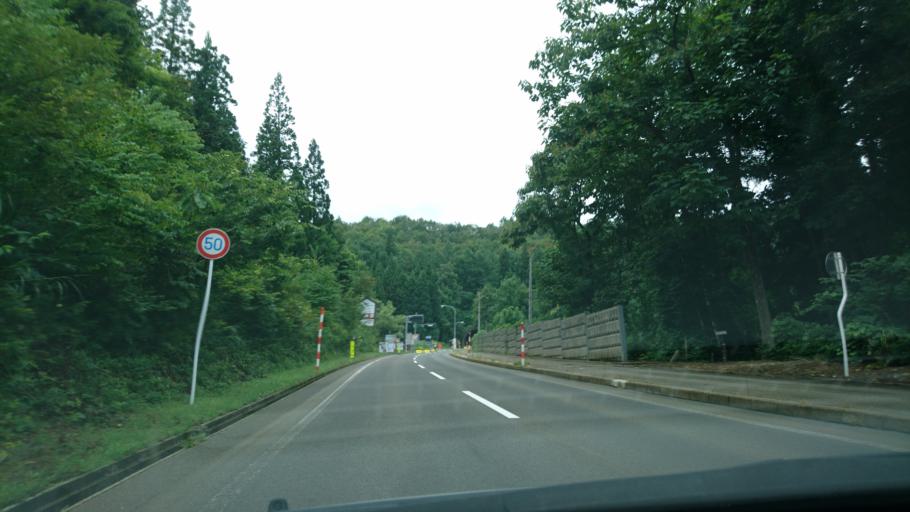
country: JP
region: Akita
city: Yuzawa
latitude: 39.1581
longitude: 140.5457
